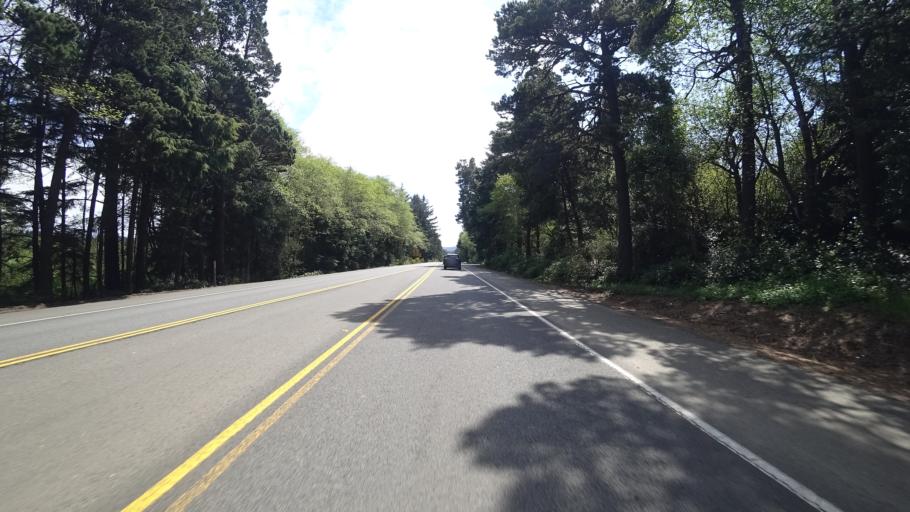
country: US
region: Oregon
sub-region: Lincoln County
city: Lincoln Beach
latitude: 44.8744
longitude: -124.0338
